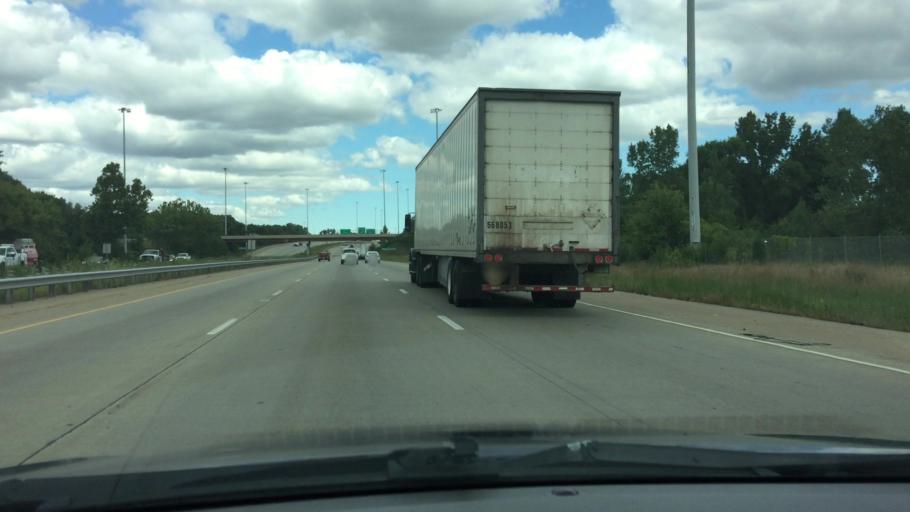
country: US
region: Illinois
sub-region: Cook County
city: Thornton
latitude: 41.5675
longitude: -87.5834
